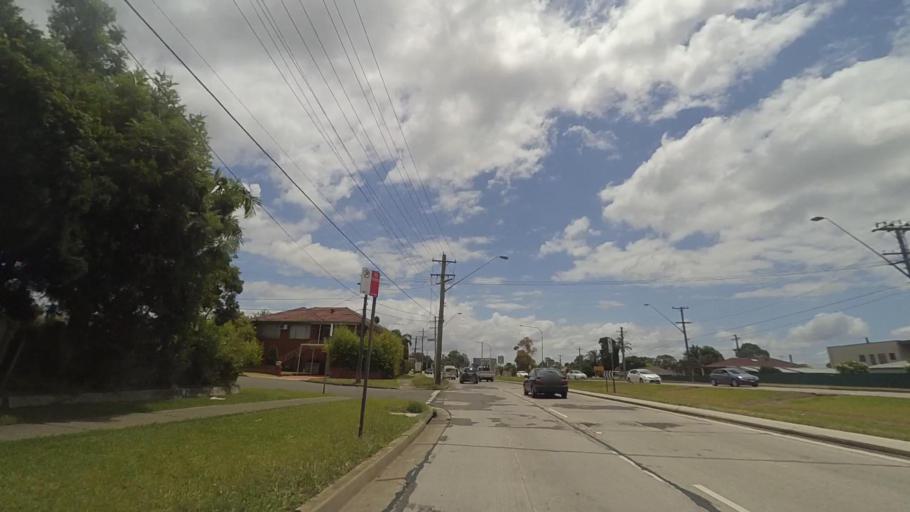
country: AU
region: New South Wales
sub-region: Fairfield
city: Cabramatta West
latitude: -33.8908
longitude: 150.9228
